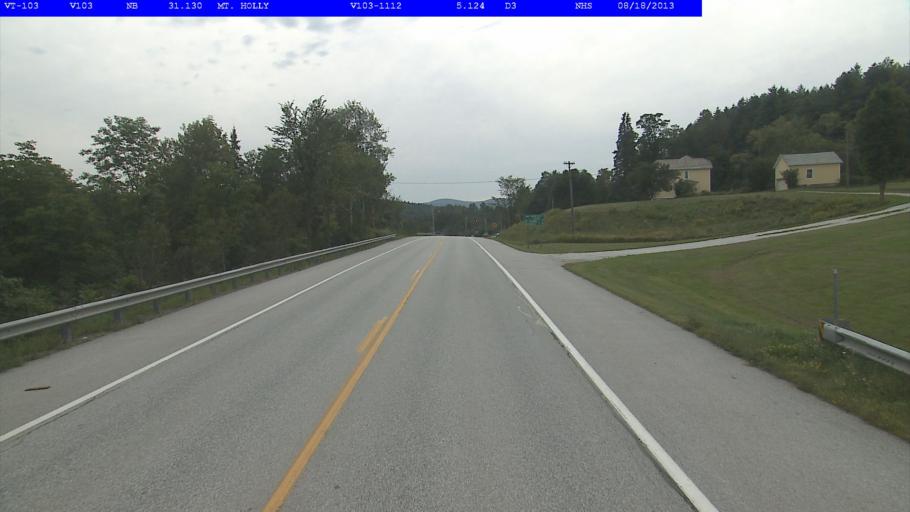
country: US
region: Vermont
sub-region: Rutland County
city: Rutland
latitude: 43.4478
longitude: -72.8231
